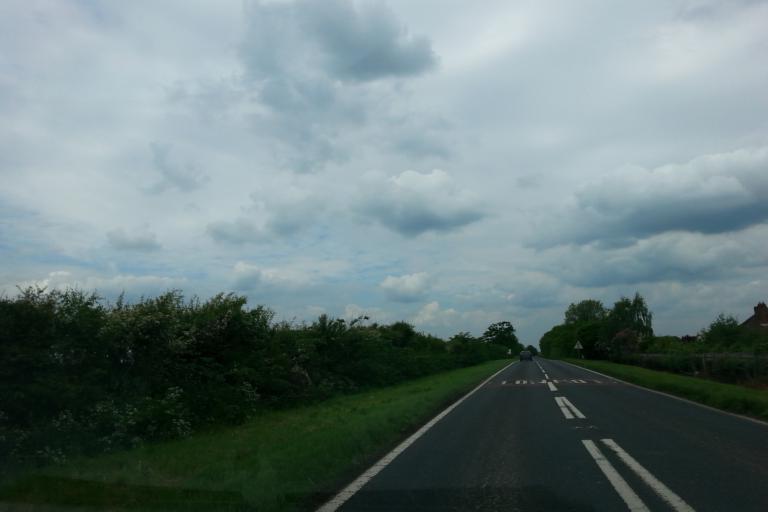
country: GB
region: England
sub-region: Cambridgeshire
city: Ramsey
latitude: 52.4180
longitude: -0.1074
